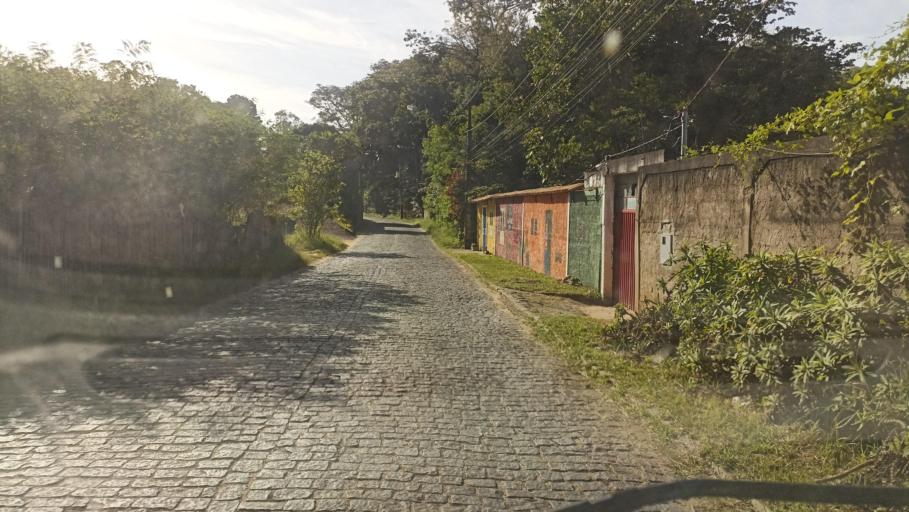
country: BR
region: Minas Gerais
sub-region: Tiradentes
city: Tiradentes
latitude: -21.1193
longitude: -44.1981
